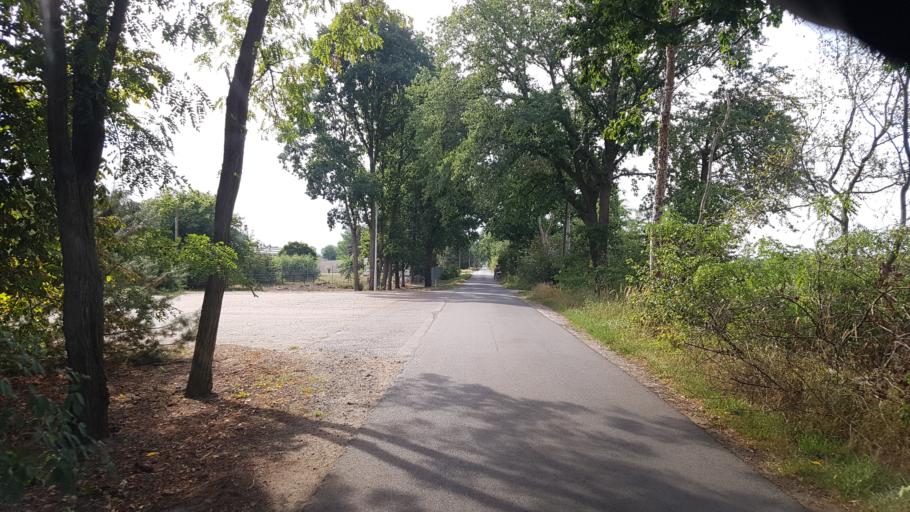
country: DE
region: Brandenburg
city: Plessa
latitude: 51.4414
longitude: 13.5972
